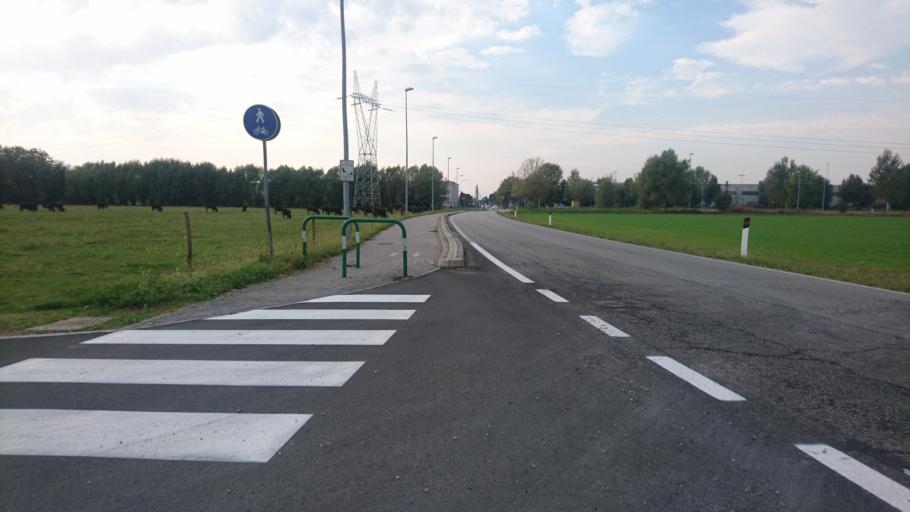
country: IT
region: Veneto
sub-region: Provincia di Padova
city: Gazzo
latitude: 45.5793
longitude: 11.6929
